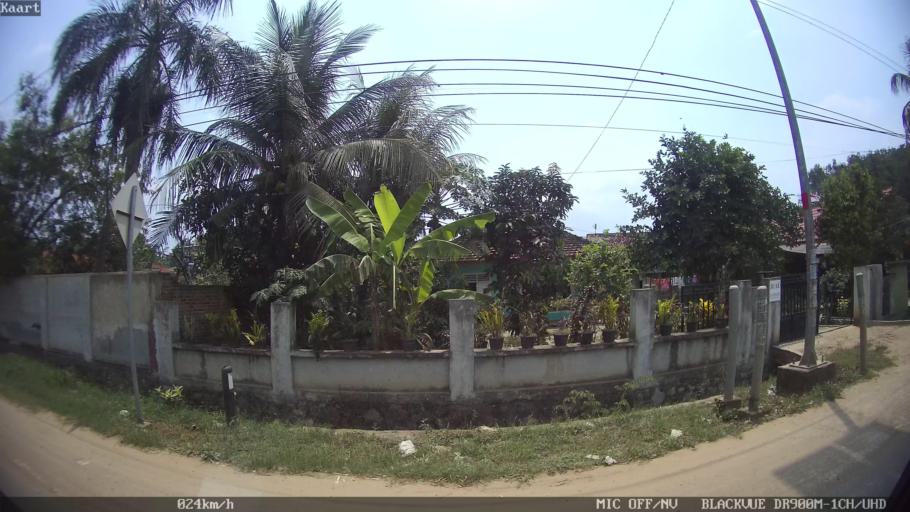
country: ID
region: Lampung
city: Gadingrejo
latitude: -5.3829
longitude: 105.0160
